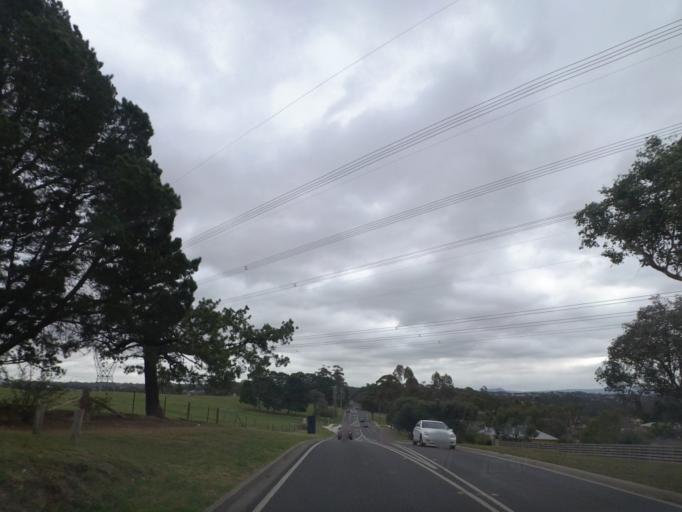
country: AU
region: Victoria
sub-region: Nillumbik
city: Eltham North
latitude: -37.6840
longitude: 145.1434
